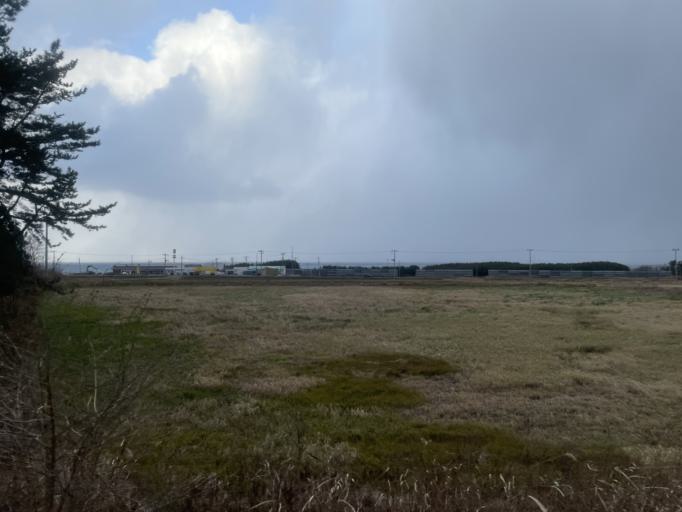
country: JP
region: Aomori
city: Mutsu
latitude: 41.1231
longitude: 141.2631
